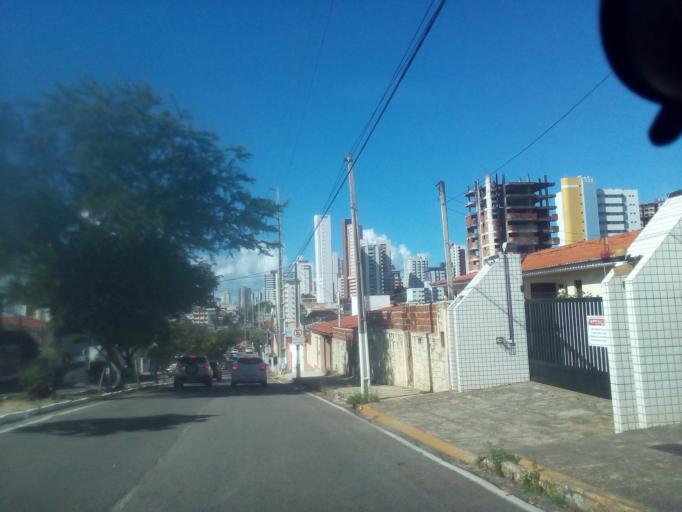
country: BR
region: Rio Grande do Norte
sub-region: Natal
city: Natal
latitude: -5.8085
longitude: -35.2069
